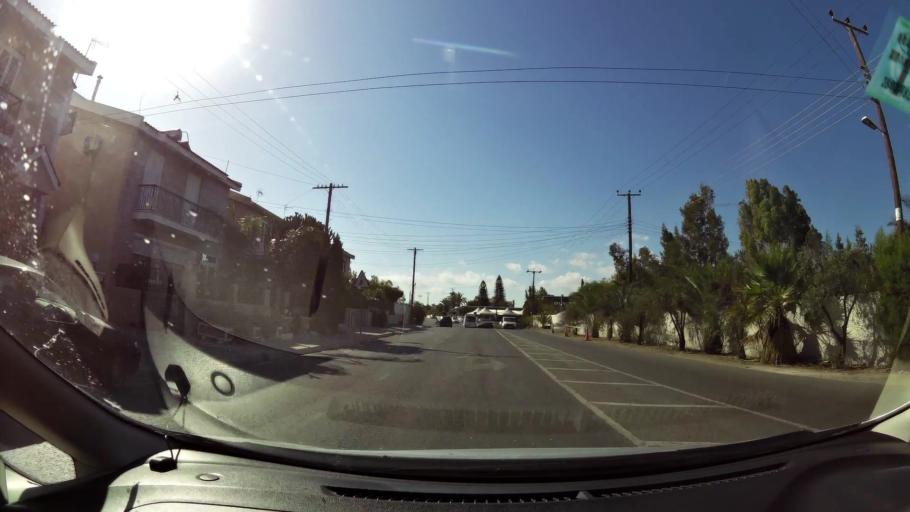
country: CY
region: Lefkosia
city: Tseri
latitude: 35.1241
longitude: 33.3439
